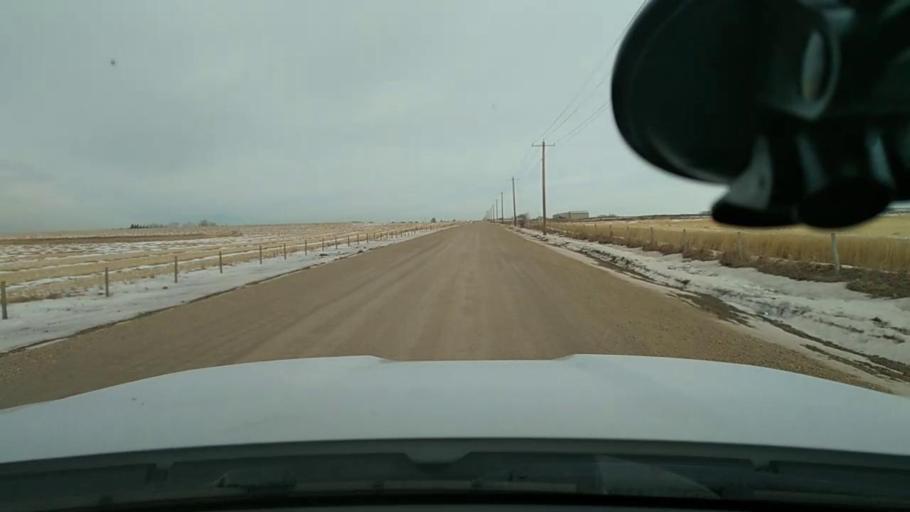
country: CA
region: Alberta
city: Airdrie
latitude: 51.2184
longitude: -113.9118
